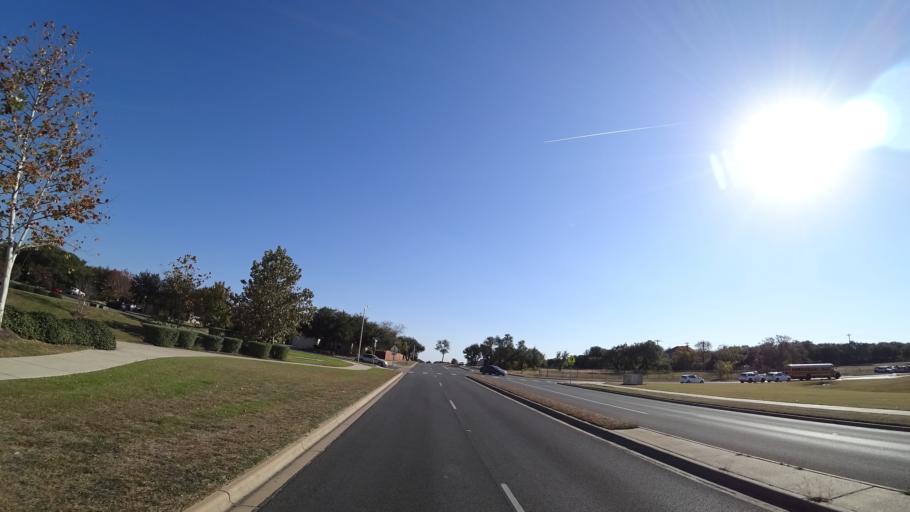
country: US
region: Texas
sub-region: Williamson County
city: Cedar Park
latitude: 30.5213
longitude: -97.8539
